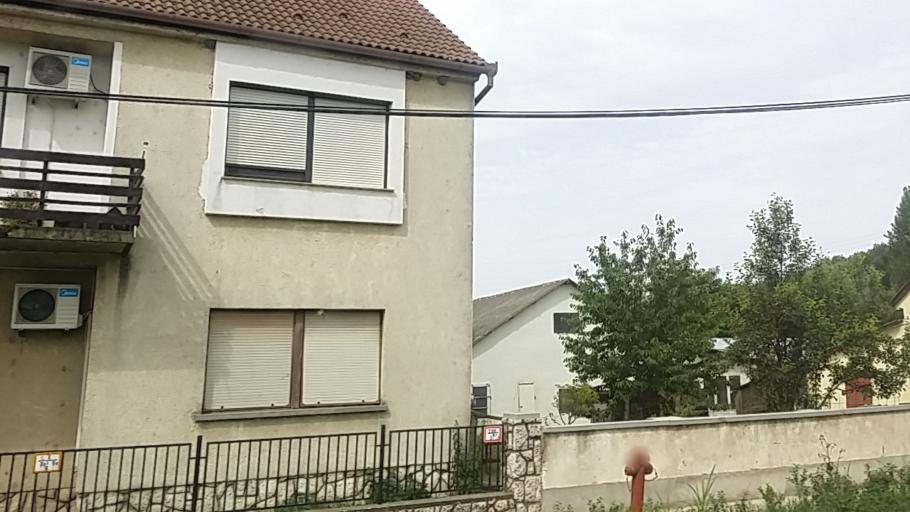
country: HU
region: Baranya
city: Boly
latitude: 45.9350
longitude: 18.4665
